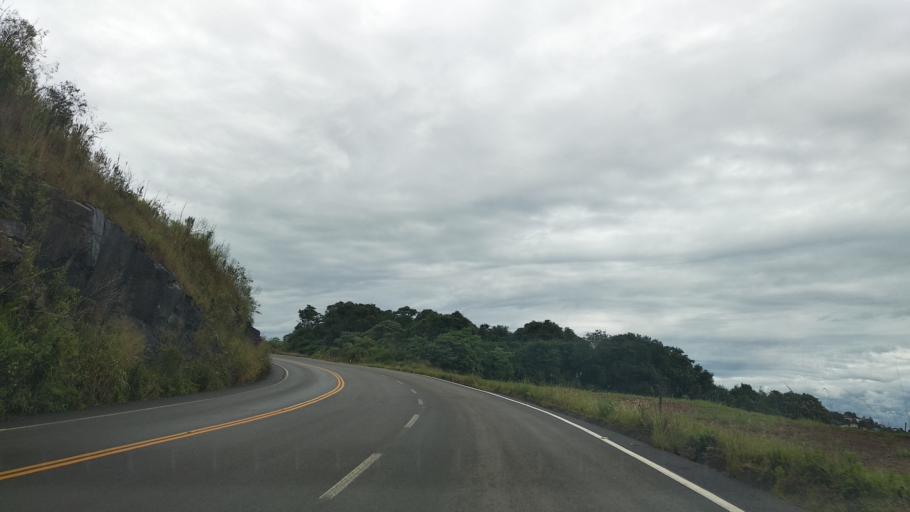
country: BR
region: Santa Catarina
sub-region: Videira
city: Videira
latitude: -27.0045
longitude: -51.1742
